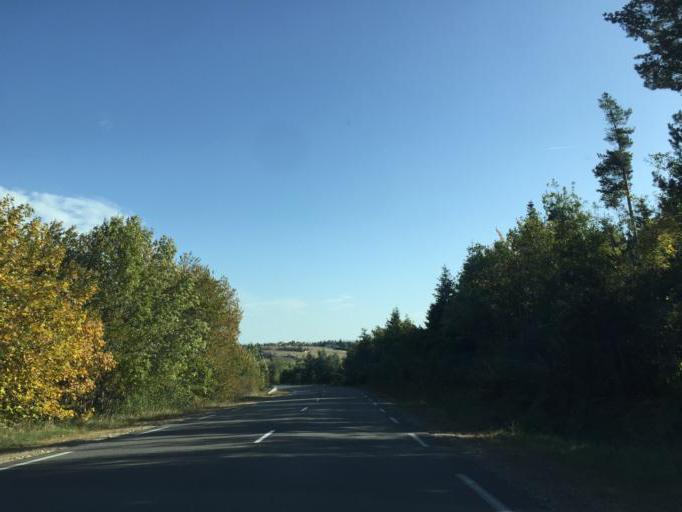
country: FR
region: Rhone-Alpes
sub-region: Departement de la Loire
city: Saint-Bonnet-le-Chateau
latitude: 45.4558
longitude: 4.1019
